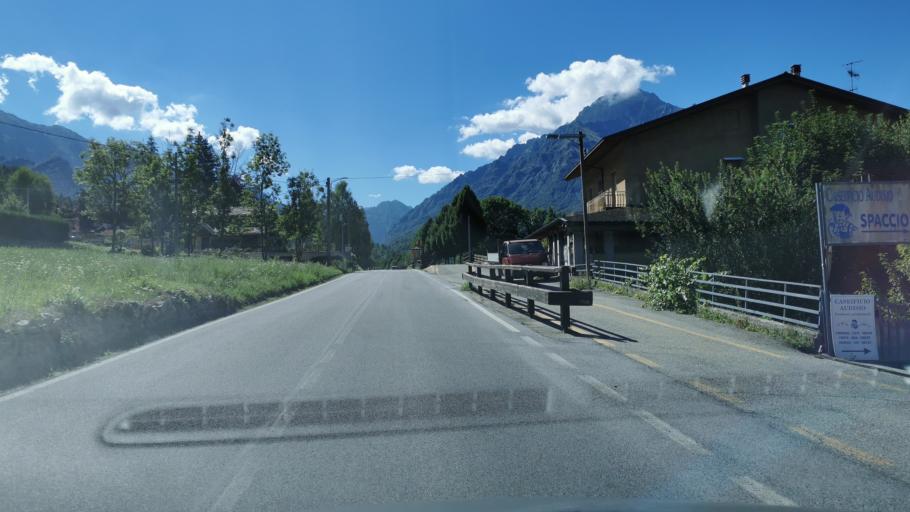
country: IT
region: Piedmont
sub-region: Provincia di Cuneo
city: Entracque
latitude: 44.2470
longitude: 7.3936
